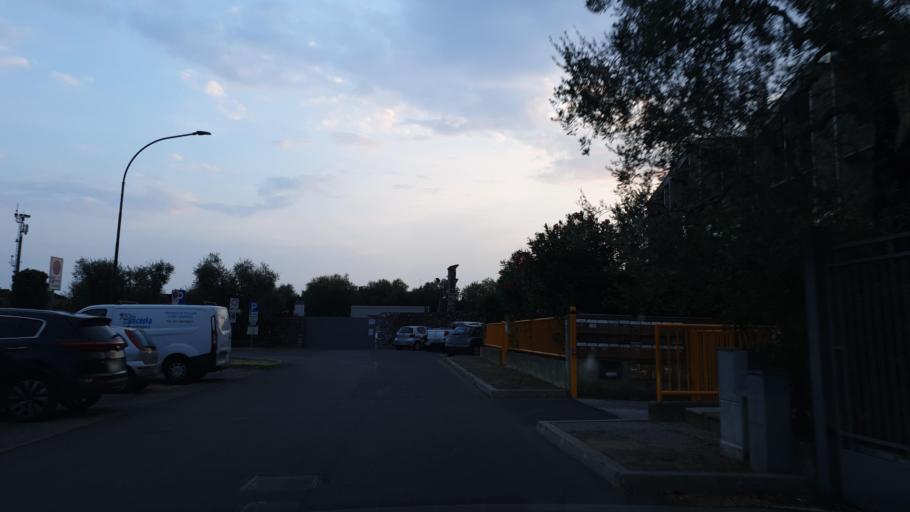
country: IT
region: Lombardy
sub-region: Provincia di Brescia
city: Toscolano Maderno
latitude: 45.6380
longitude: 10.6176
